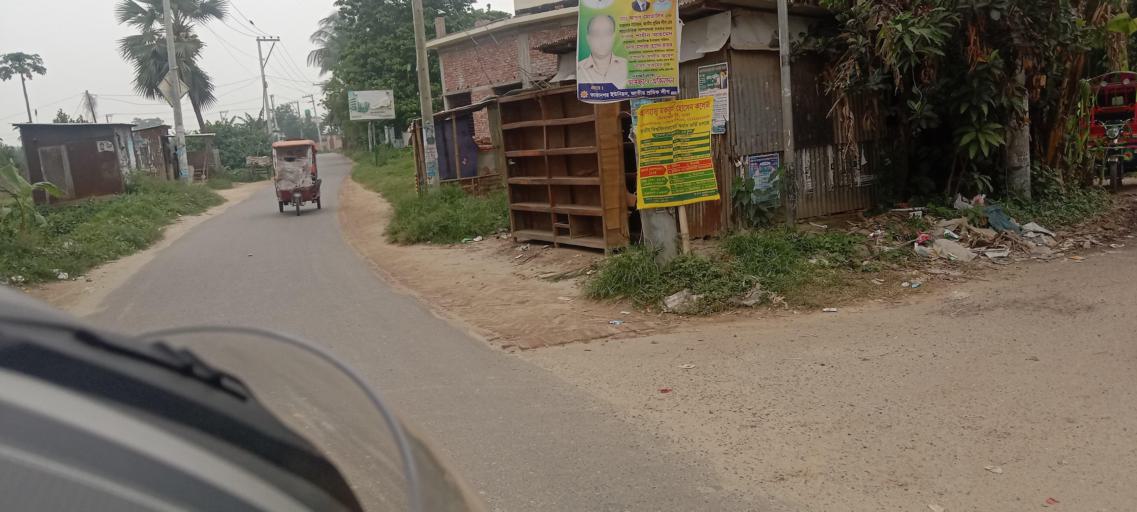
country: BD
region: Dhaka
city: Azimpur
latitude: 23.7371
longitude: 90.3192
